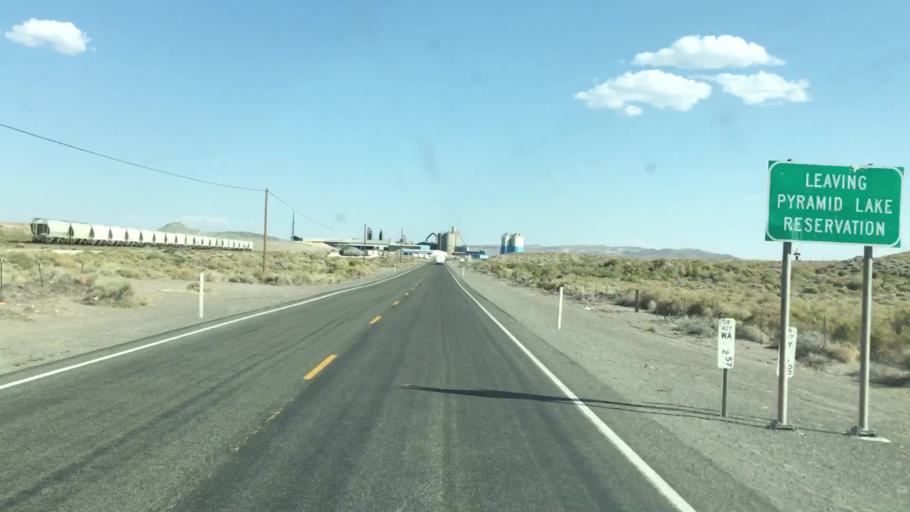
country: US
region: Nevada
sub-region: Lyon County
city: Fernley
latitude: 39.6271
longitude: -119.2731
